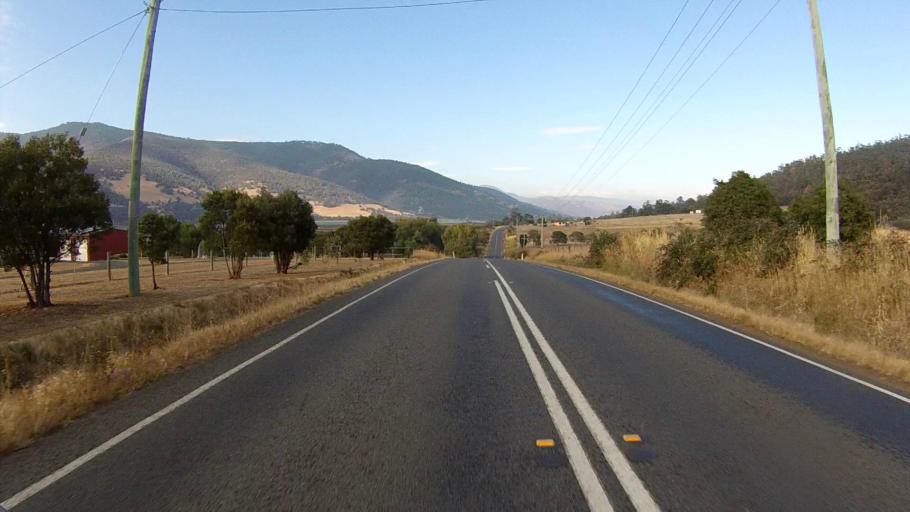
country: AU
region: Tasmania
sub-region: Brighton
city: Bridgewater
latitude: -42.7364
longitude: 147.1745
